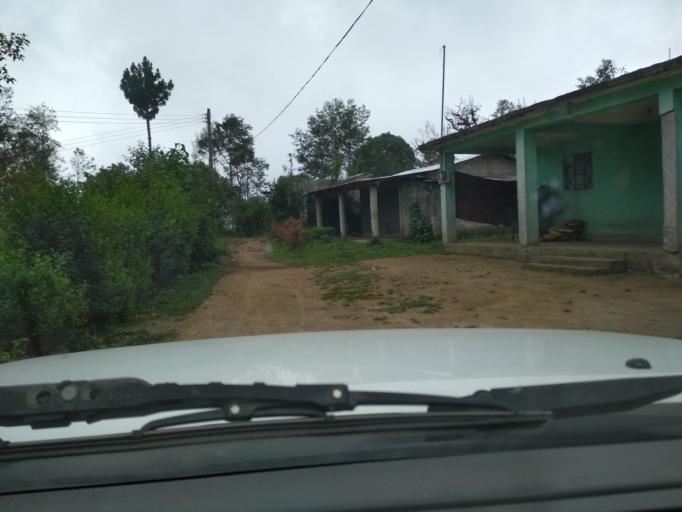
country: MX
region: Veracruz
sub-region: La Perla
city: Chilapa
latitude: 18.9865
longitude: -97.1564
